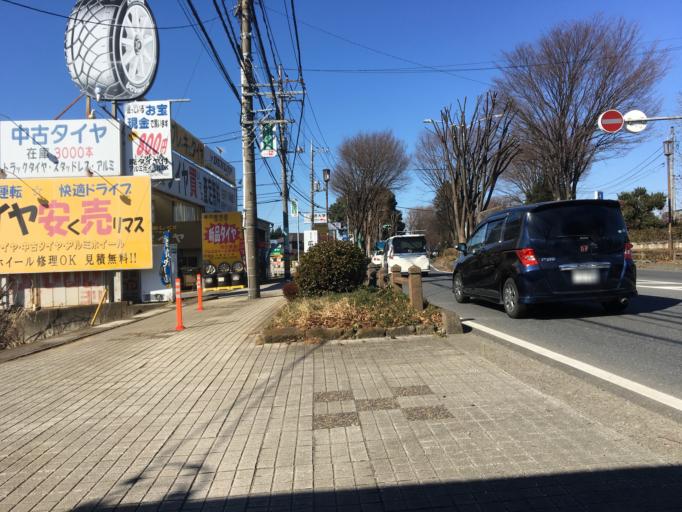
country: JP
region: Saitama
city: Oi
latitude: 35.8205
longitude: 139.5408
